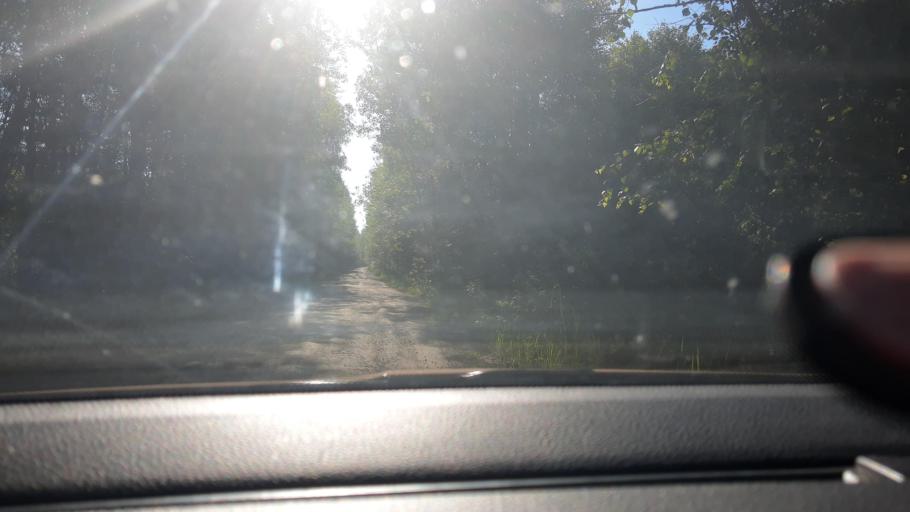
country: RU
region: Moskovskaya
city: Elektrogorsk
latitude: 55.8935
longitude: 38.7207
